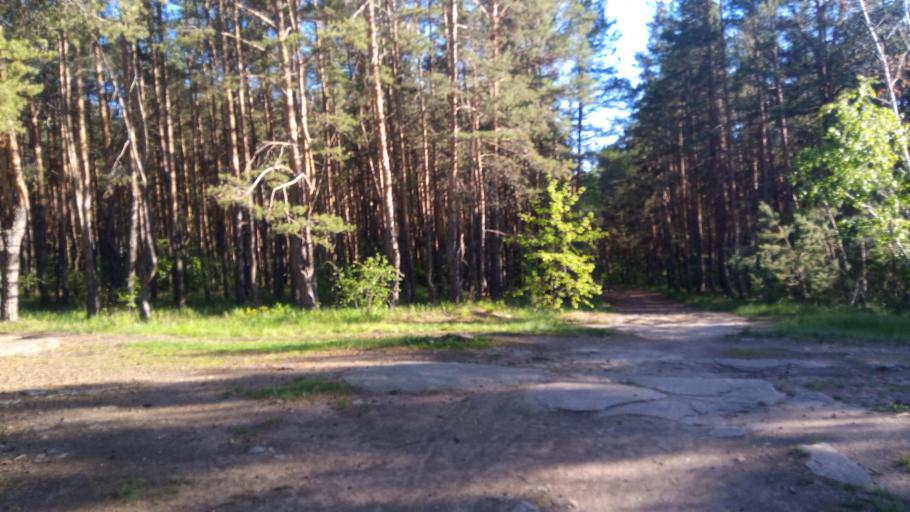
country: RU
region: Chelyabinsk
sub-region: Gorod Chelyabinsk
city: Chelyabinsk
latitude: 55.1343
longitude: 61.3348
